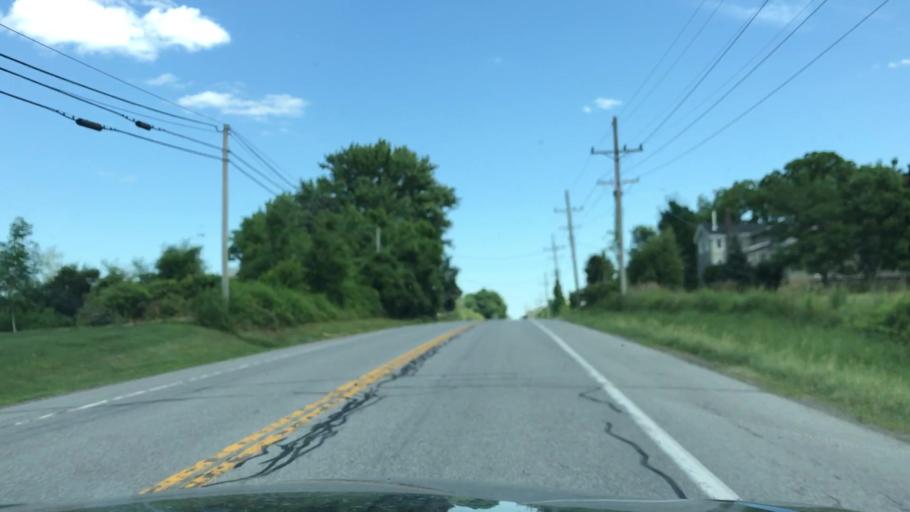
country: US
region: New York
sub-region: Wyoming County
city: Perry
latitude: 42.7472
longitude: -78.0245
